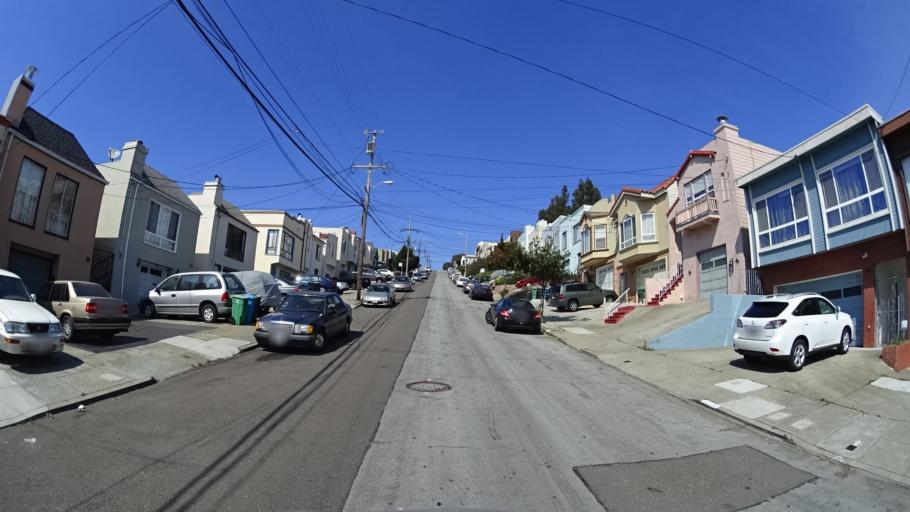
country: US
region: California
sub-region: San Mateo County
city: Daly City
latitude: 37.7148
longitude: -122.4689
